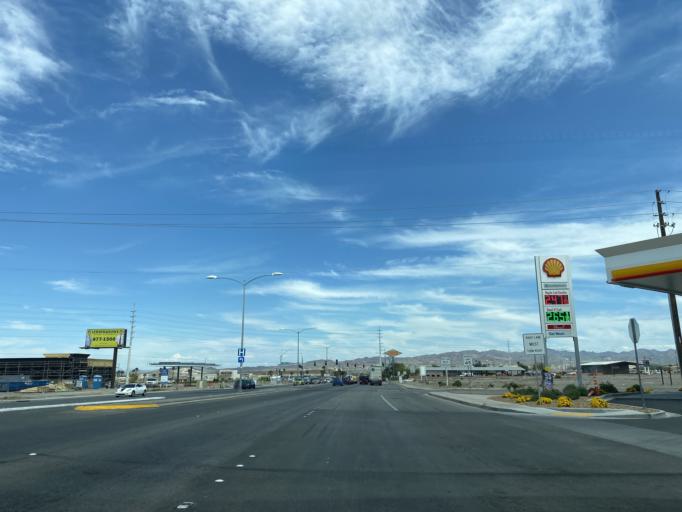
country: US
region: Nevada
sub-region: Clark County
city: Henderson
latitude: 36.0637
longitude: -115.0295
